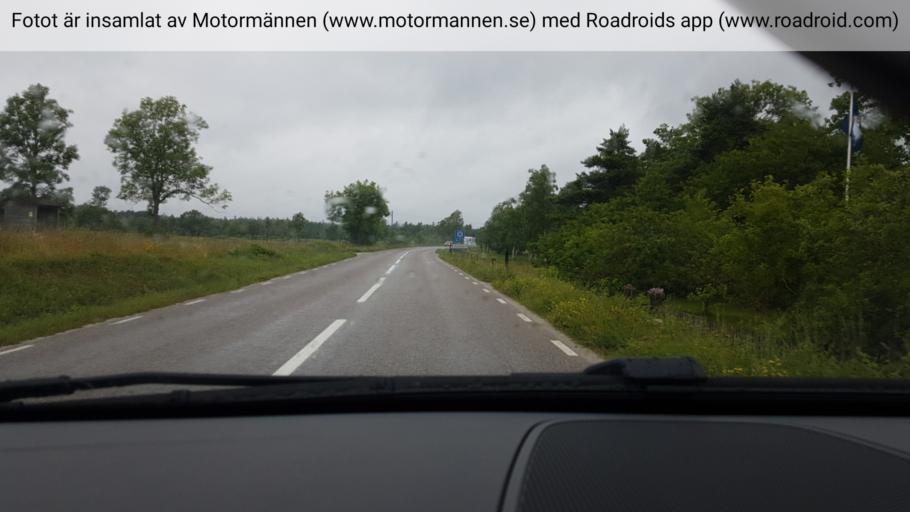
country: SE
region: Gotland
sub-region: Gotland
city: Slite
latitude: 57.6714
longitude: 18.7746
